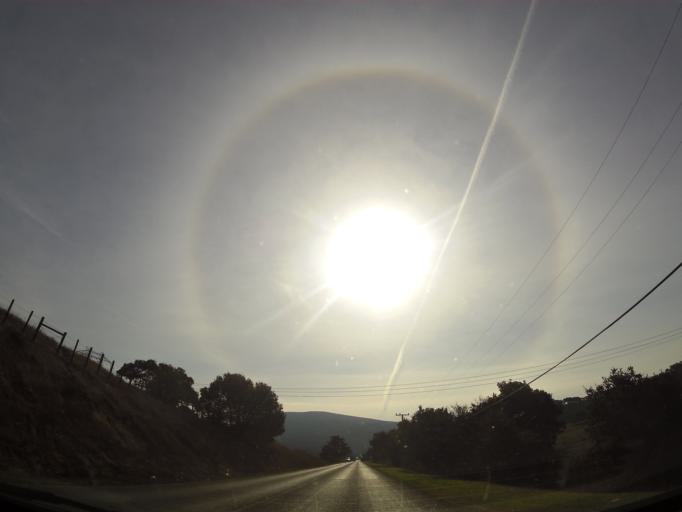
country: US
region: California
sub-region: Monterey County
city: Prunedale
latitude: 36.7836
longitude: -121.6104
